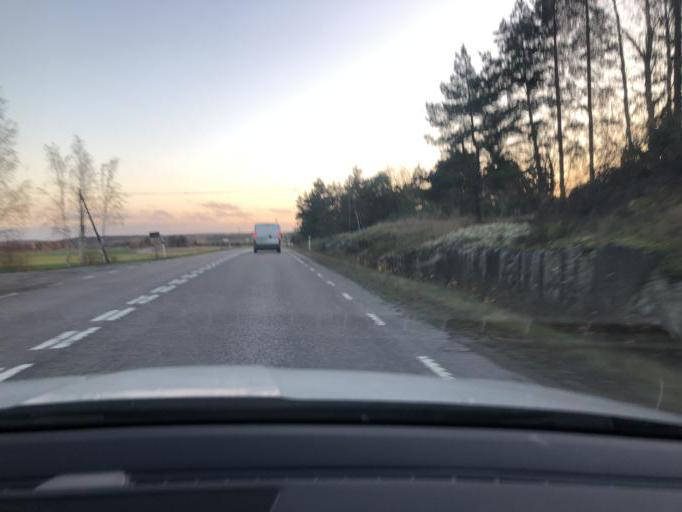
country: SE
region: Soedermanland
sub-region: Strangnas Kommun
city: Akers Styckebruk
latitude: 59.2906
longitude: 17.1082
